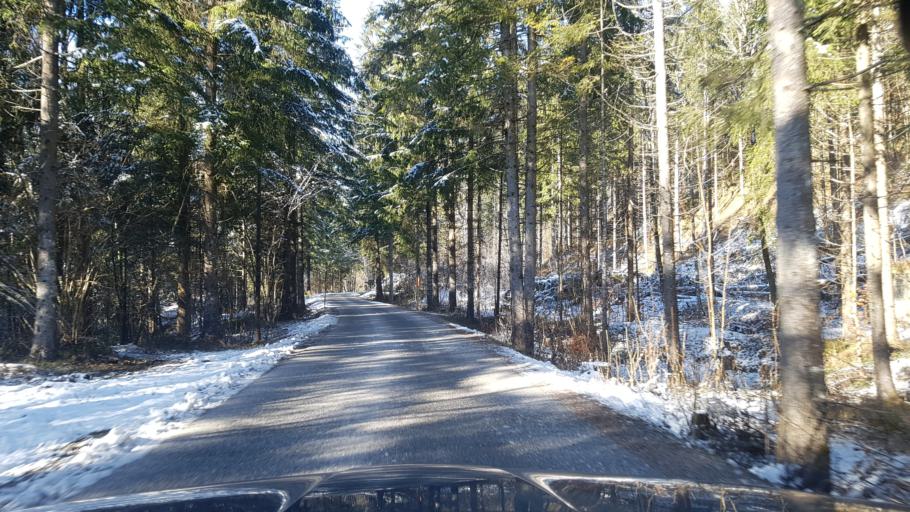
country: AT
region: Salzburg
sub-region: Politischer Bezirk Salzburg-Umgebung
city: Faistenau
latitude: 47.7686
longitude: 13.2249
